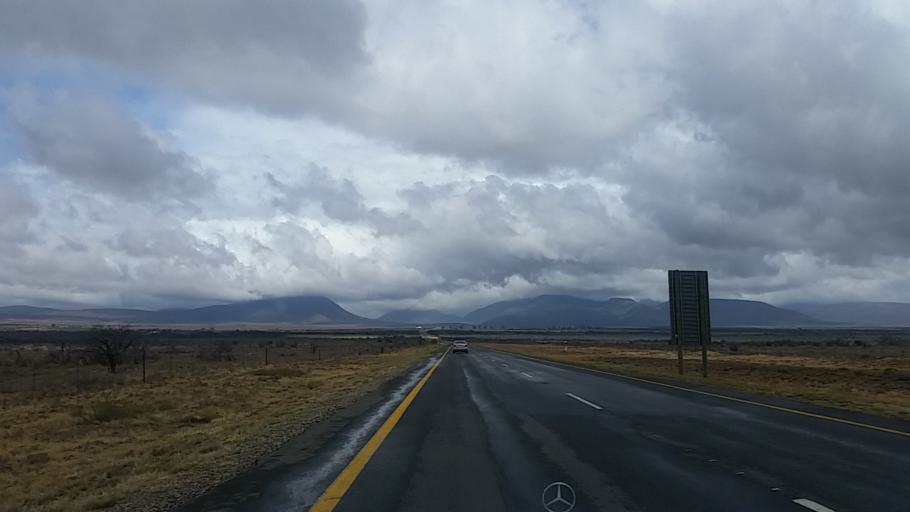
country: ZA
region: Eastern Cape
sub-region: Cacadu District Municipality
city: Graaff-Reinet
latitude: -32.1506
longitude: 24.5764
